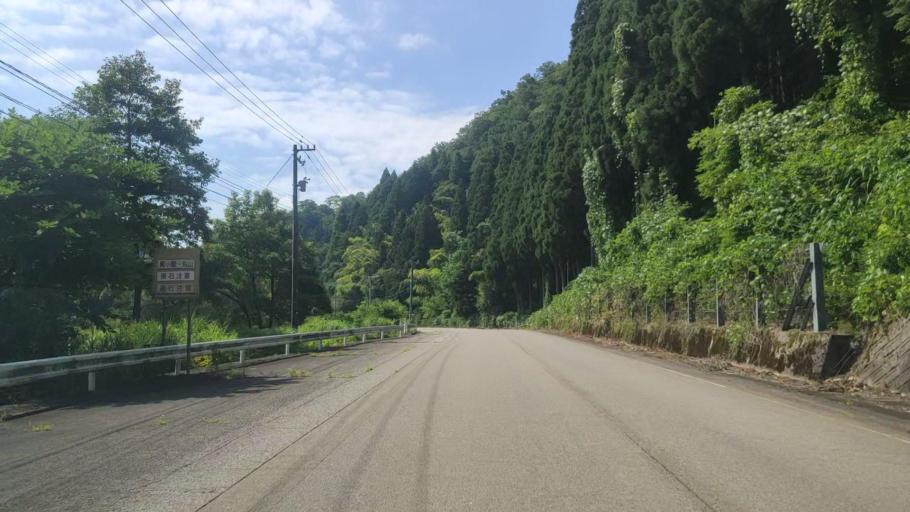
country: JP
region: Ishikawa
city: Komatsu
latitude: 36.3263
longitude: 136.5289
